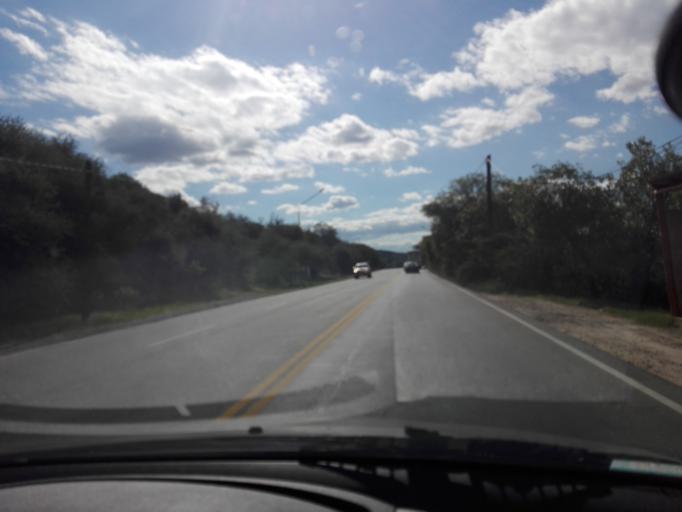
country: AR
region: Cordoba
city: Villa Las Rosas
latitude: -31.8748
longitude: -64.9803
